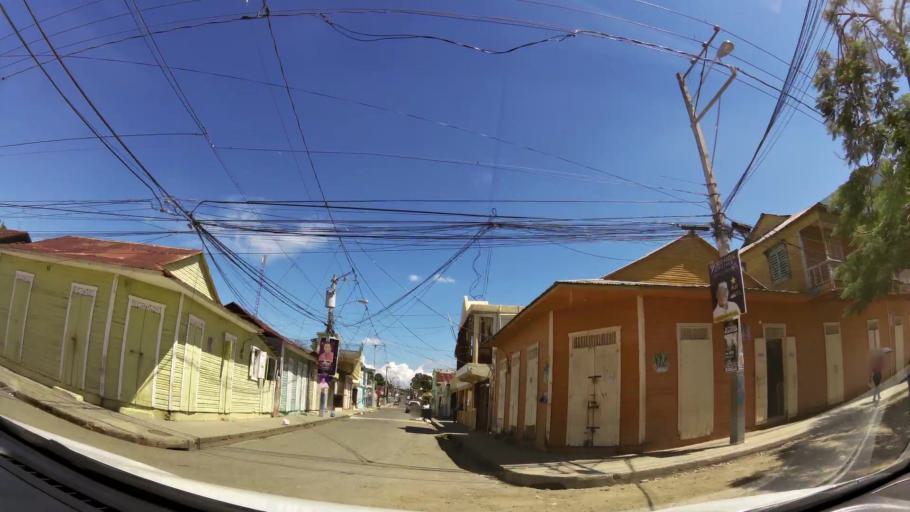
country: DO
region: Santiago
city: Santiago de los Caballeros
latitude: 19.4472
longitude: -70.7007
